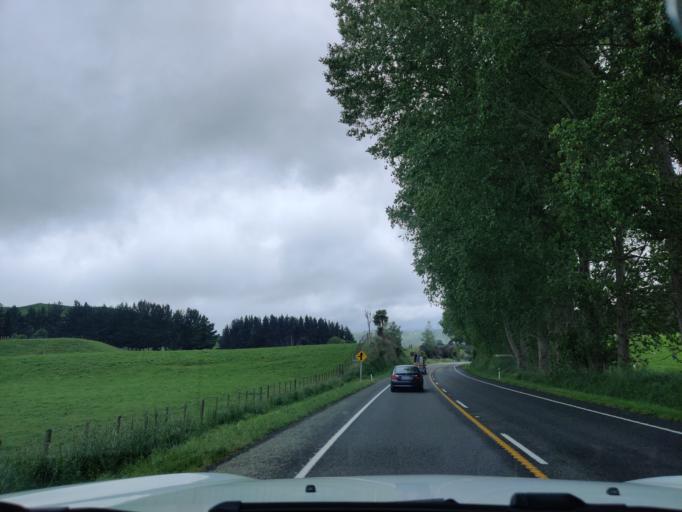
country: NZ
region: Manawatu-Wanganui
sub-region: Ruapehu District
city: Waiouru
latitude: -39.6487
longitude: 175.7684
